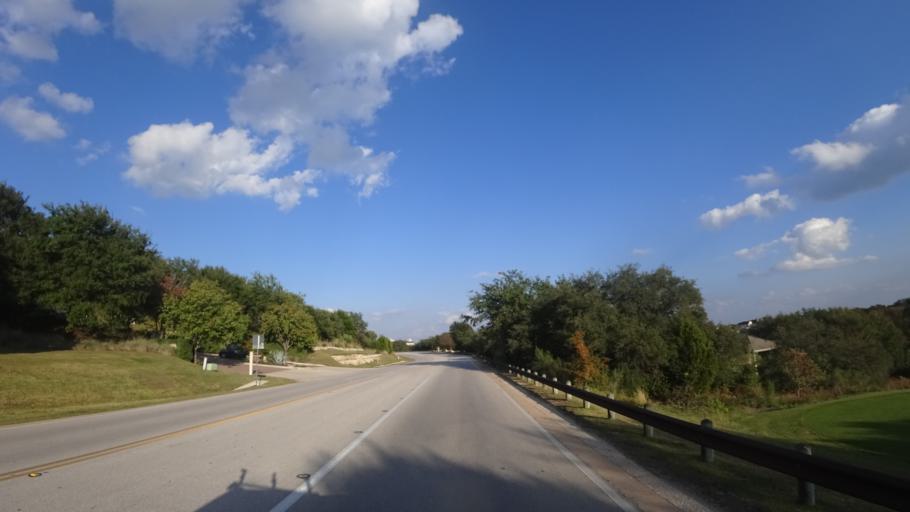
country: US
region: Texas
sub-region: Travis County
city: Barton Creek
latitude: 30.2895
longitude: -97.8651
